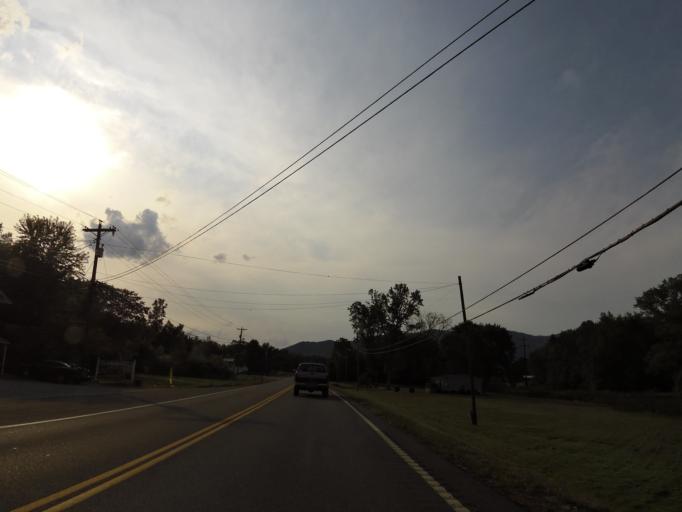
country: US
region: Tennessee
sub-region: Morgan County
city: Coalfield
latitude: 36.0604
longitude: -84.4456
